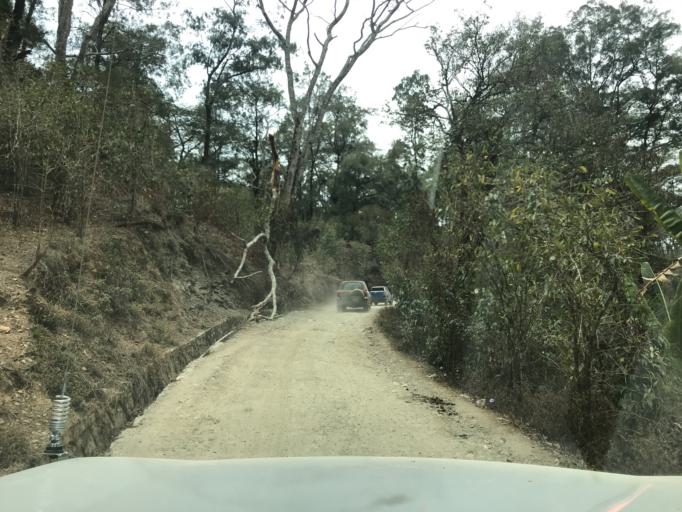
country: TL
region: Ermera
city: Gleno
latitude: -8.8357
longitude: 125.4489
